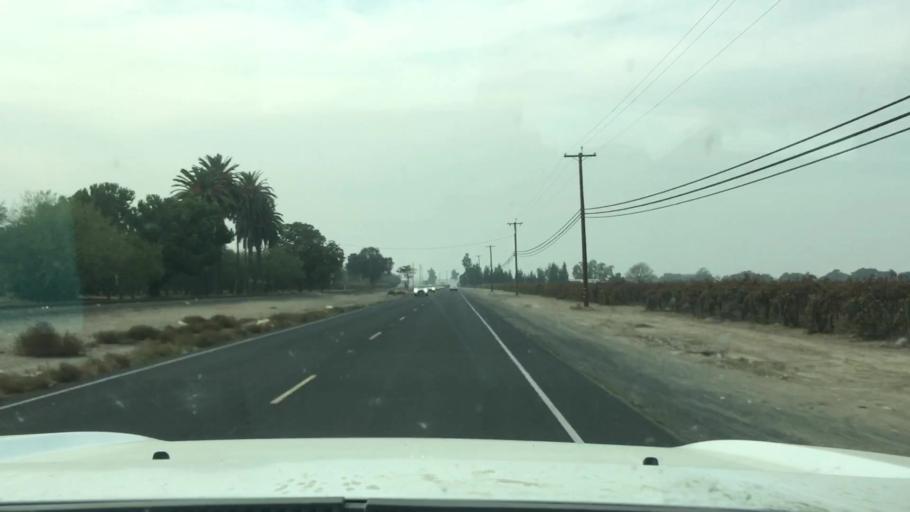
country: US
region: California
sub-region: San Joaquin County
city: Manteca
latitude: 37.8498
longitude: -121.1911
